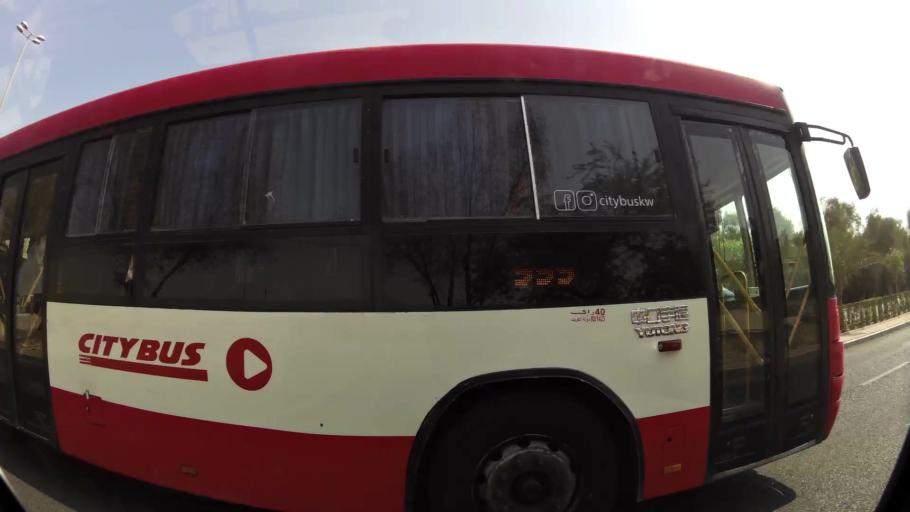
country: KW
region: Al Ahmadi
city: Al Fintas
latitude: 29.1610
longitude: 48.1218
